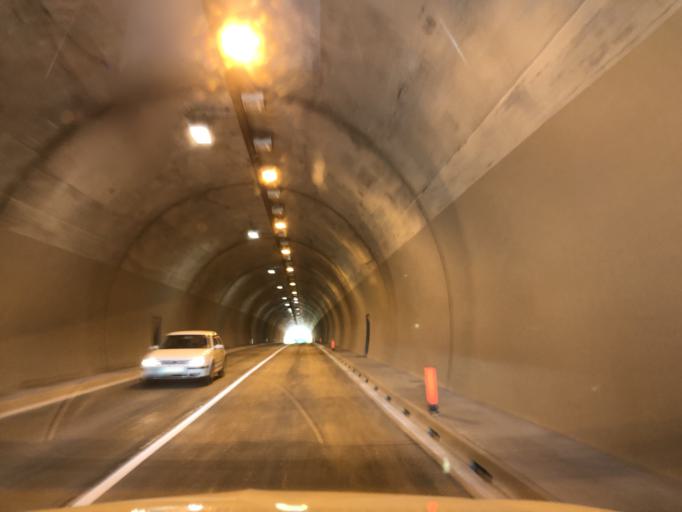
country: SI
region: Nova Gorica
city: Solkan
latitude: 45.9700
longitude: 13.6520
